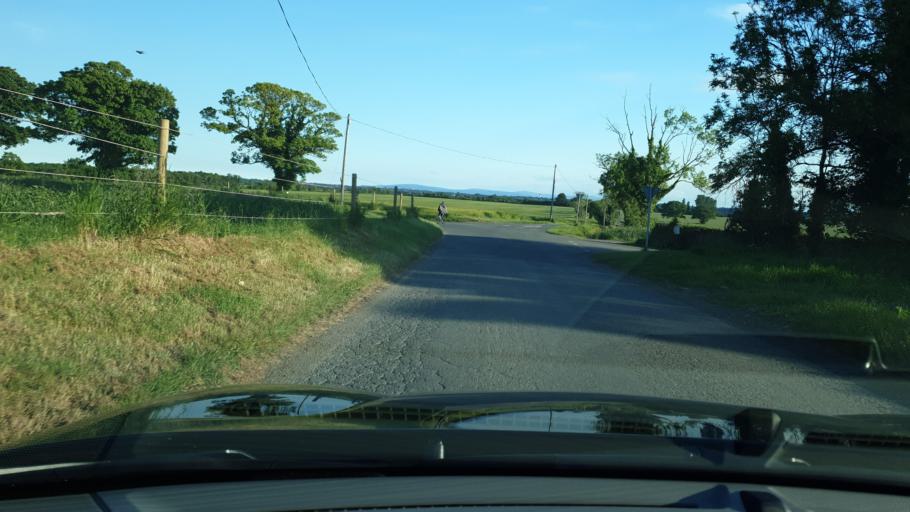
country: IE
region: Leinster
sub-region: Fingal County
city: Swords
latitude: 53.5039
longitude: -6.2403
